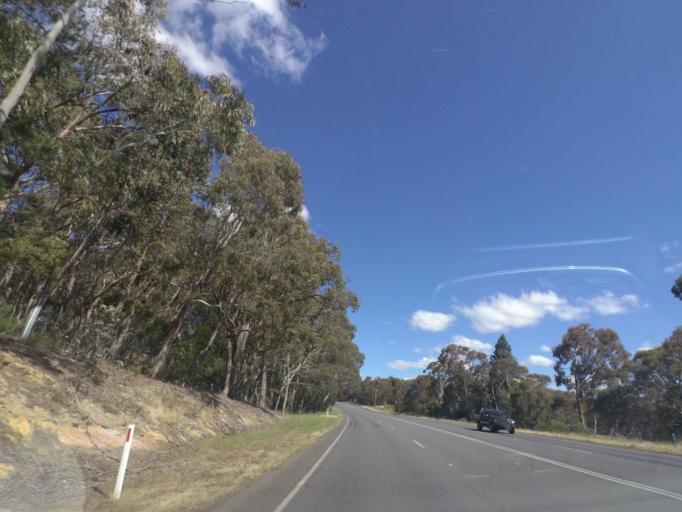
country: AU
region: Victoria
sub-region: Hume
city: Sunbury
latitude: -37.4396
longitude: 144.5653
